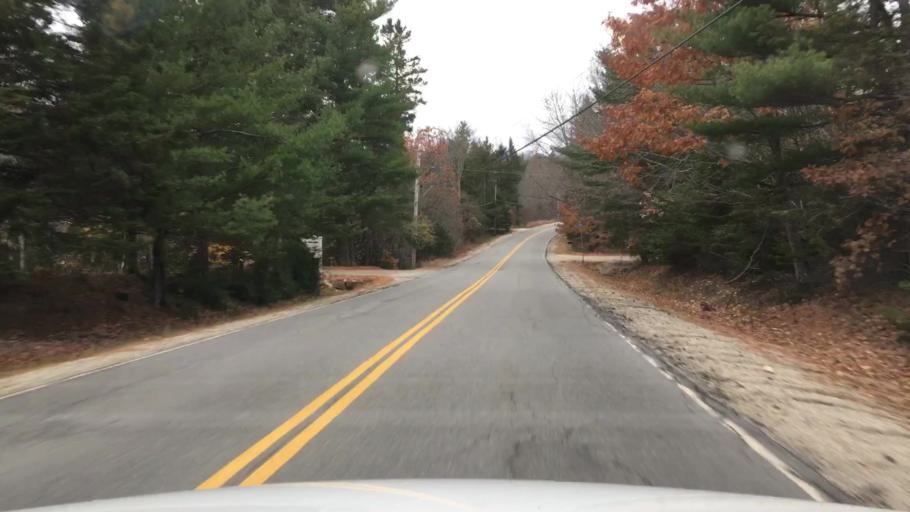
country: US
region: Maine
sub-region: Hancock County
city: Penobscot
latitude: 44.4313
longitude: -68.6284
